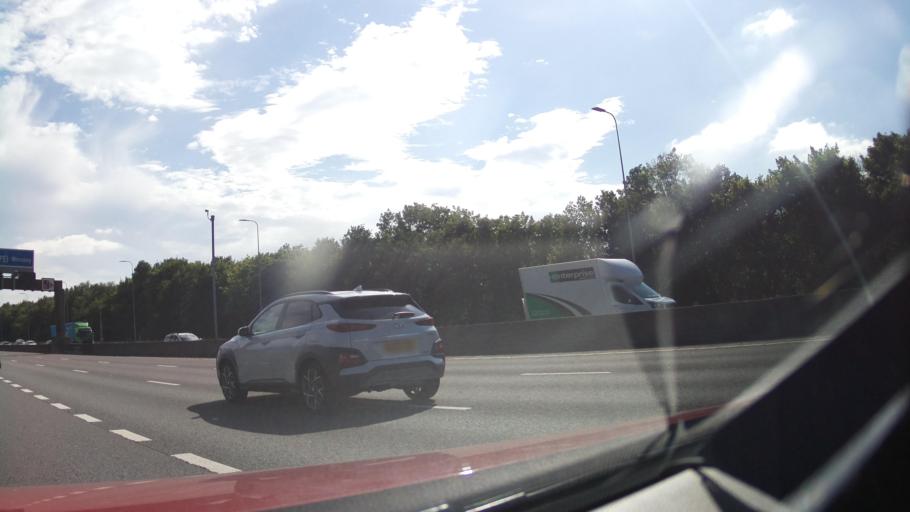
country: GB
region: England
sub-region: Borough of Bolton
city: Kearsley
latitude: 53.5180
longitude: -2.3683
